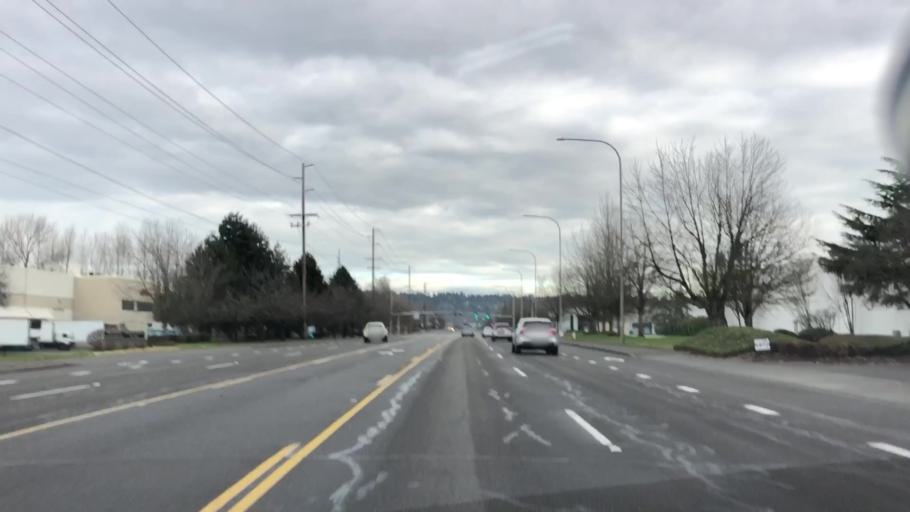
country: US
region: Washington
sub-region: King County
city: Kent
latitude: 47.4123
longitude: -122.2470
